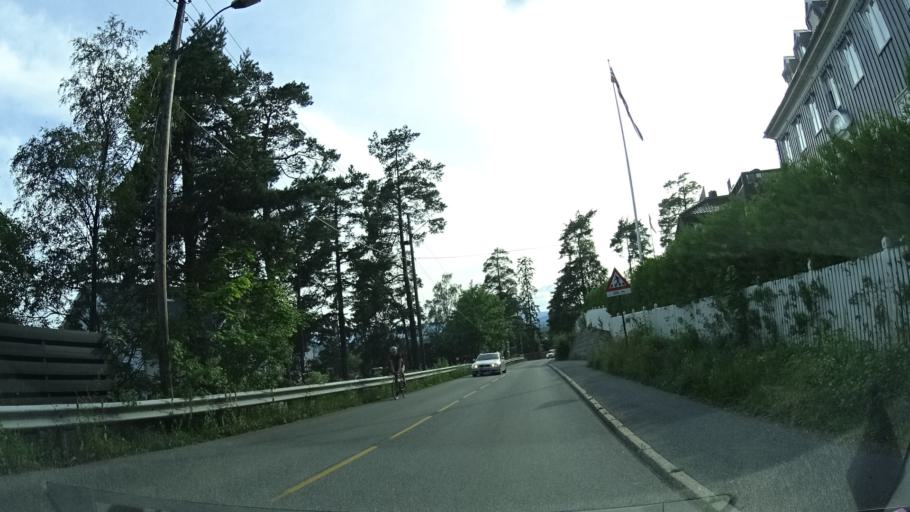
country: NO
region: Oslo
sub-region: Oslo
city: Sjolyststranda
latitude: 59.9571
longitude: 10.6730
